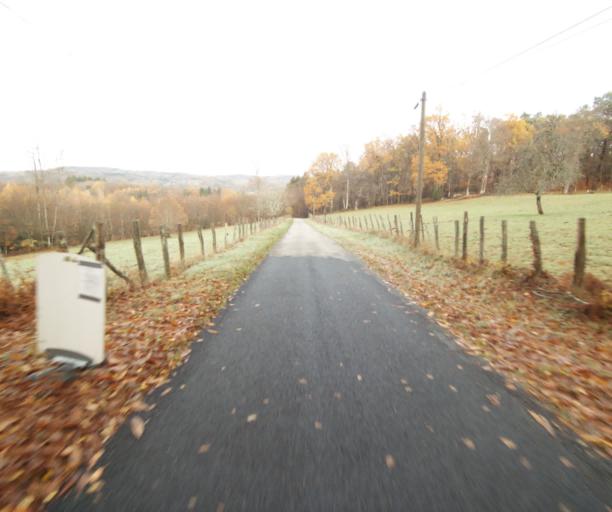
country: FR
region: Limousin
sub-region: Departement de la Correze
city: Cornil
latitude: 45.2065
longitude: 1.7125
